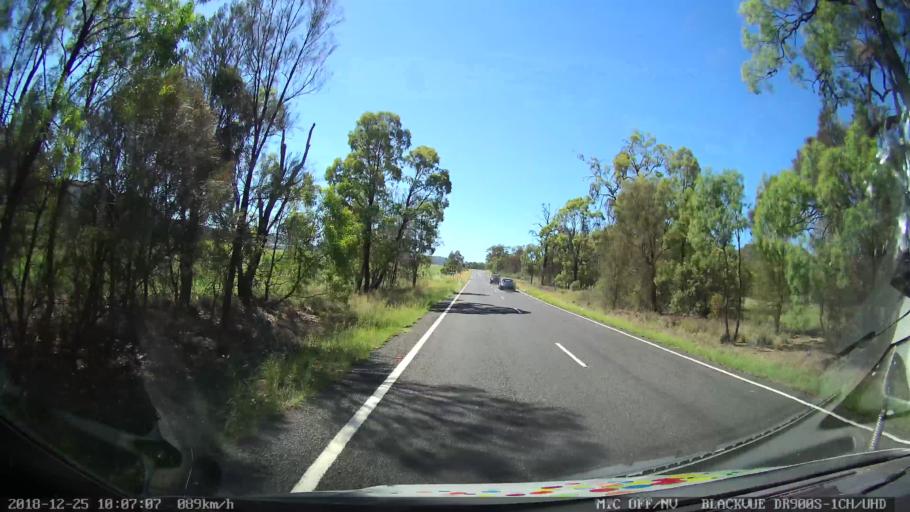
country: AU
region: New South Wales
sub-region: Upper Hunter Shire
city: Merriwa
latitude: -32.2675
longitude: 150.4954
